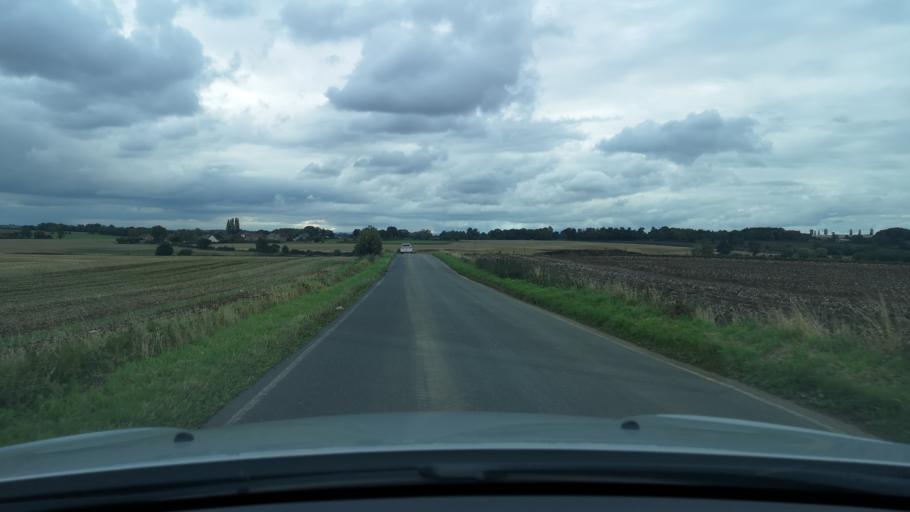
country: GB
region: England
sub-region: City and Borough of Wakefield
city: Darrington
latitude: 53.6685
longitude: -1.2907
